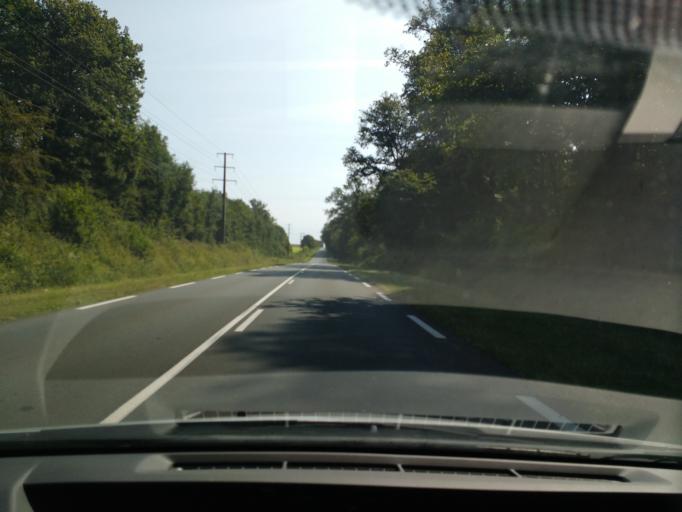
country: FR
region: Pays de la Loire
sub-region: Departement de Maine-et-Loire
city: Bauge-en-Anjou
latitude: 47.5323
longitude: -0.0577
